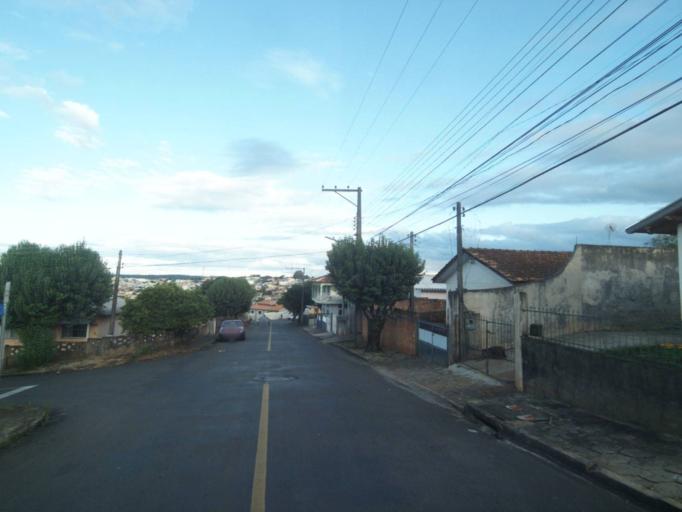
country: BR
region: Parana
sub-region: Telemaco Borba
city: Telemaco Borba
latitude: -24.3276
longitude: -50.6369
